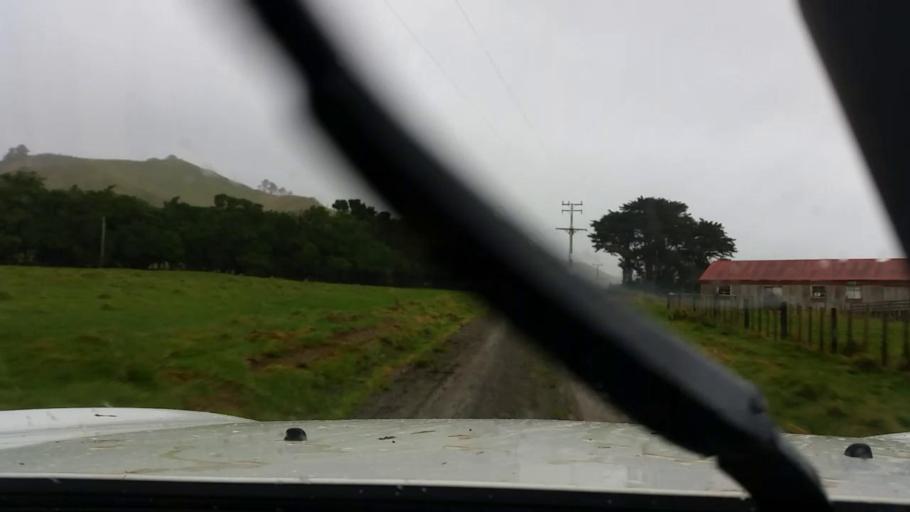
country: NZ
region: Wellington
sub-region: Masterton District
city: Masterton
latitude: -41.2627
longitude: 175.8944
